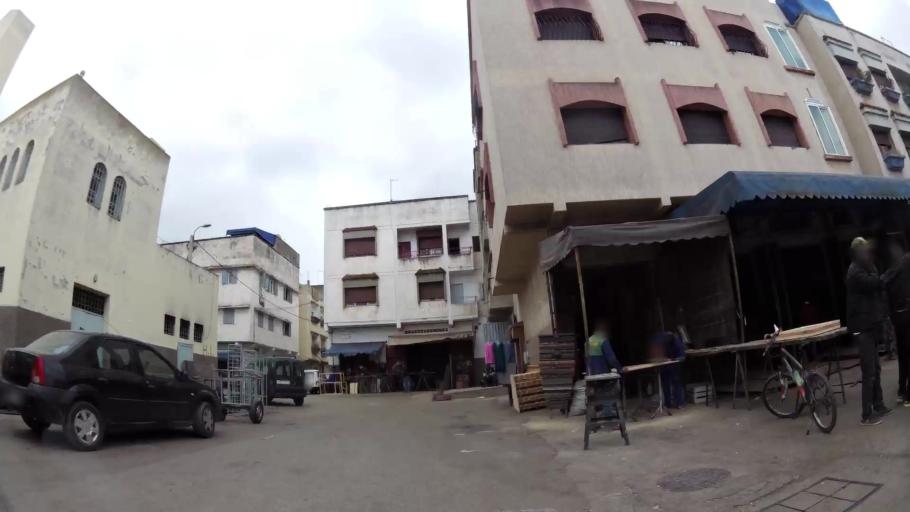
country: MA
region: Rabat-Sale-Zemmour-Zaer
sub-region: Rabat
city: Rabat
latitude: 33.9795
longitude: -6.8196
